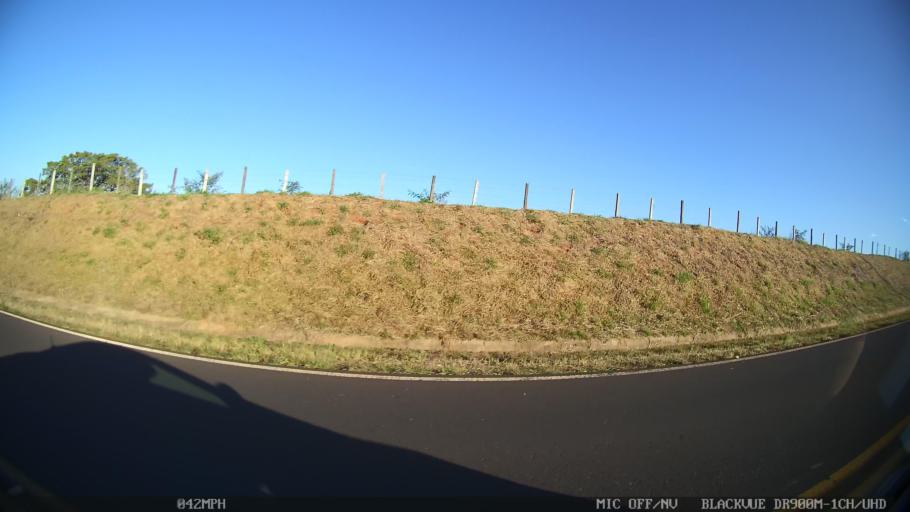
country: BR
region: Sao Paulo
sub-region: Guapiacu
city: Guapiacu
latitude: -20.7873
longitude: -49.2478
